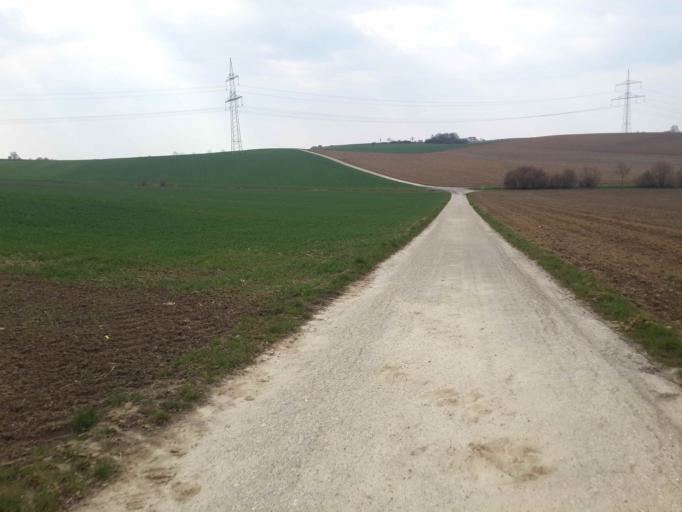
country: DE
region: Baden-Wuerttemberg
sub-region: Regierungsbezirk Stuttgart
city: Eppingen
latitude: 49.1654
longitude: 8.9136
